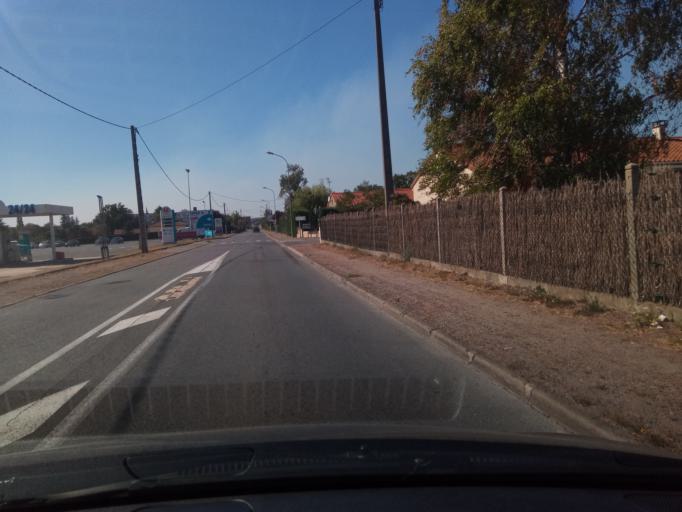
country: FR
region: Poitou-Charentes
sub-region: Departement de la Vienne
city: Montmorillon
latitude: 46.4310
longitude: 0.8857
